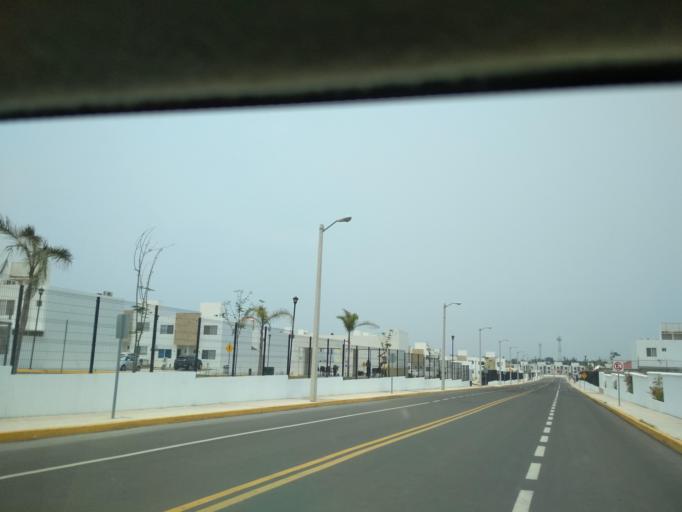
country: MX
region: Veracruz
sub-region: Veracruz
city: Las Amapolas
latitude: 19.1501
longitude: -96.2094
